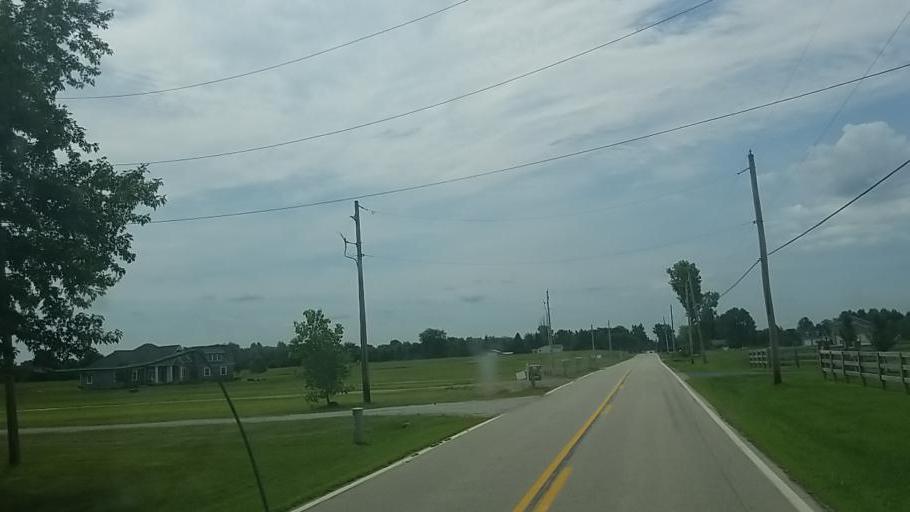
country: US
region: Ohio
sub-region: Delaware County
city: Sunbury
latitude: 40.1947
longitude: -82.8258
